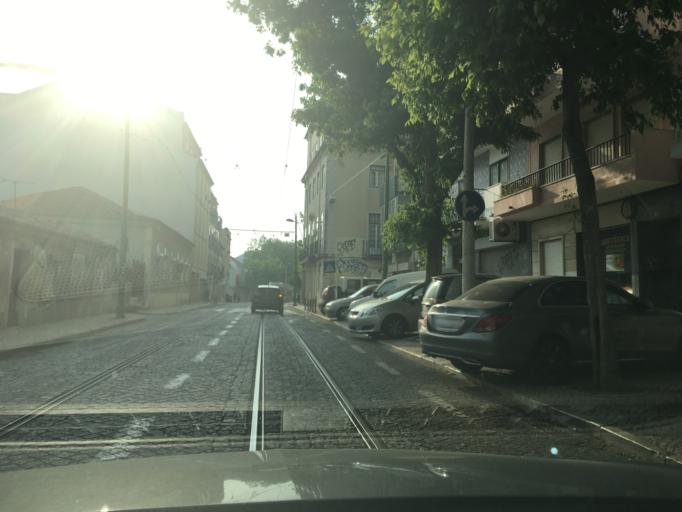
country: PT
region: Lisbon
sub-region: Oeiras
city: Alges
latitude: 38.6962
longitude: -9.2198
